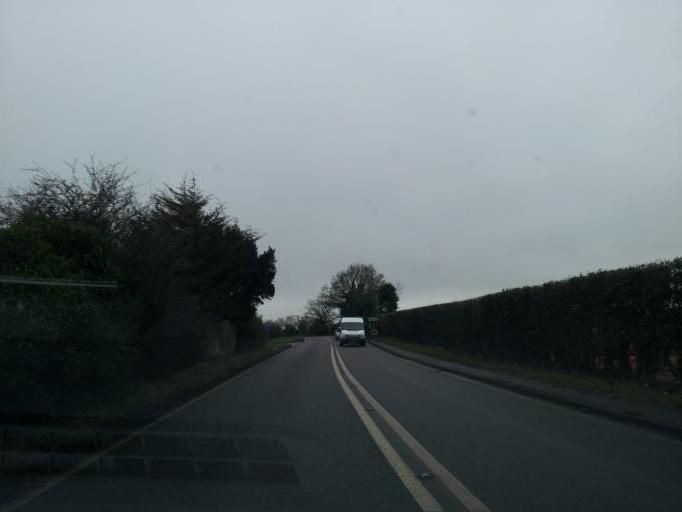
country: GB
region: England
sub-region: Essex
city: Mistley
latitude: 51.9831
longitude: 1.0968
